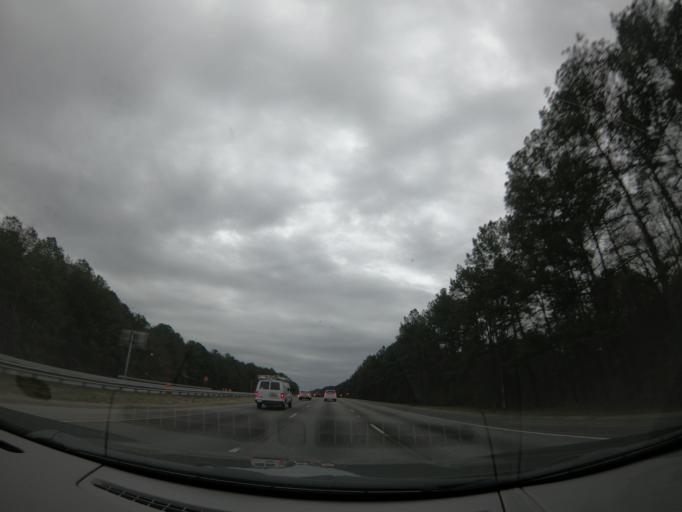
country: US
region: Georgia
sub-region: Whitfield County
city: Dalton
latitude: 34.6382
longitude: -84.9781
